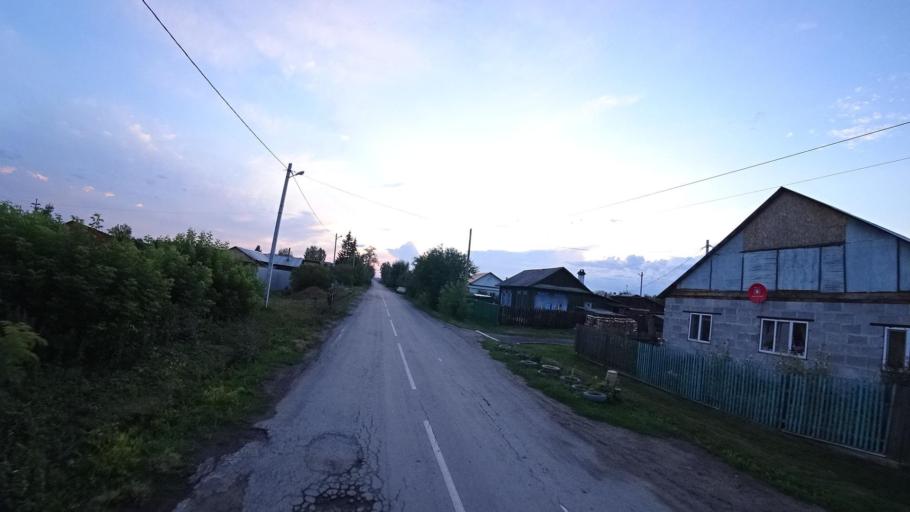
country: RU
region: Sverdlovsk
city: Kamyshlov
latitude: 56.8495
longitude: 62.7330
